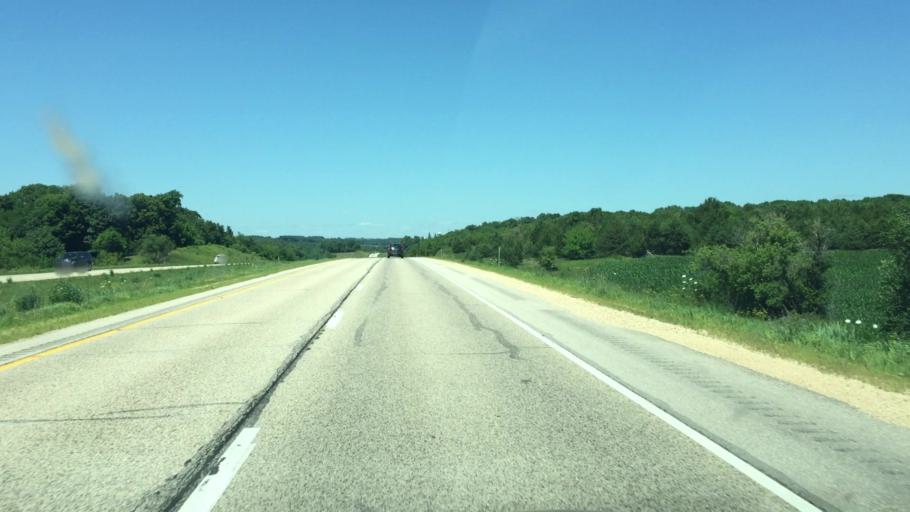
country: US
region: Iowa
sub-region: Jackson County
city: Maquoketa
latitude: 42.1380
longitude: -90.6771
